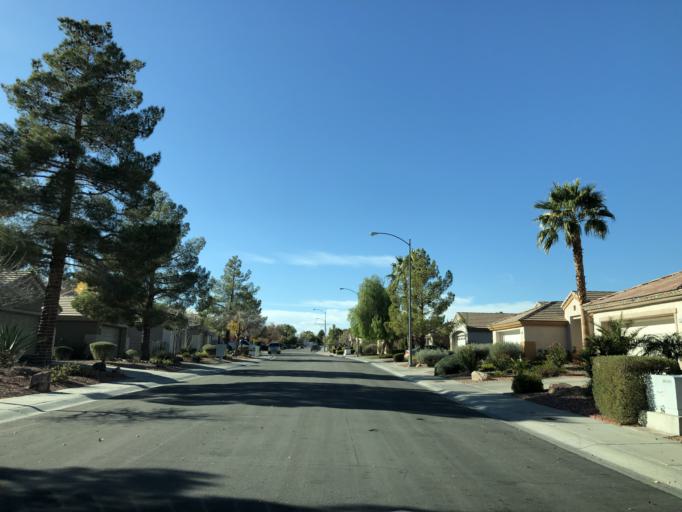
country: US
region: Nevada
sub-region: Clark County
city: Whitney
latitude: 36.0125
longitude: -115.0769
